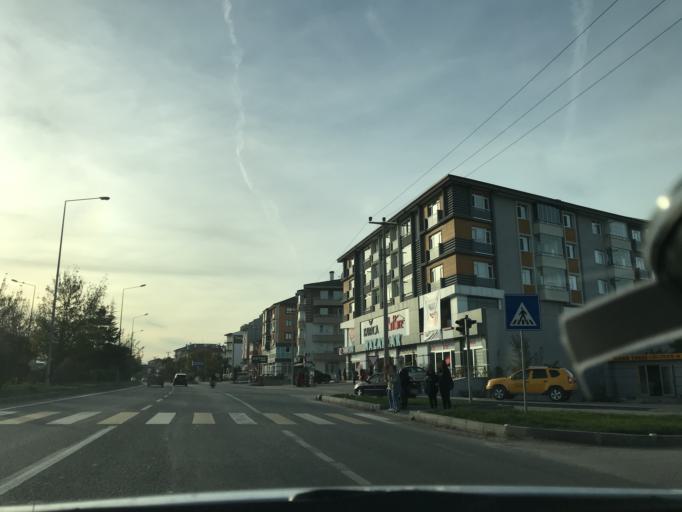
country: TR
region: Bolu
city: Bolu
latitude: 40.7391
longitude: 31.6101
